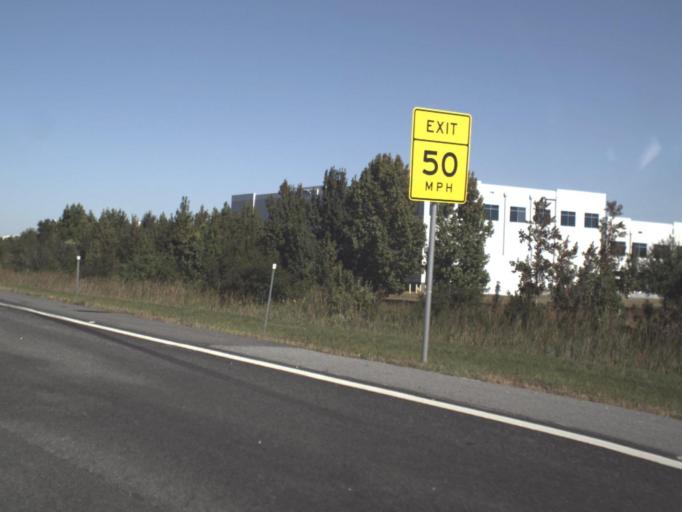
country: US
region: Florida
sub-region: Hillsborough County
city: Cheval
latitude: 28.1841
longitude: -82.5396
